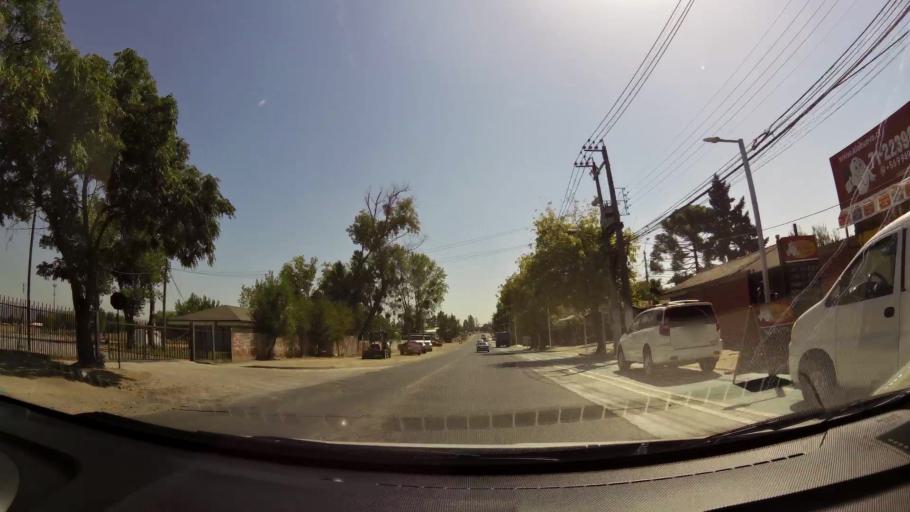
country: CL
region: Maule
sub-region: Provincia de Talca
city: Talca
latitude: -35.4267
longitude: -71.6391
